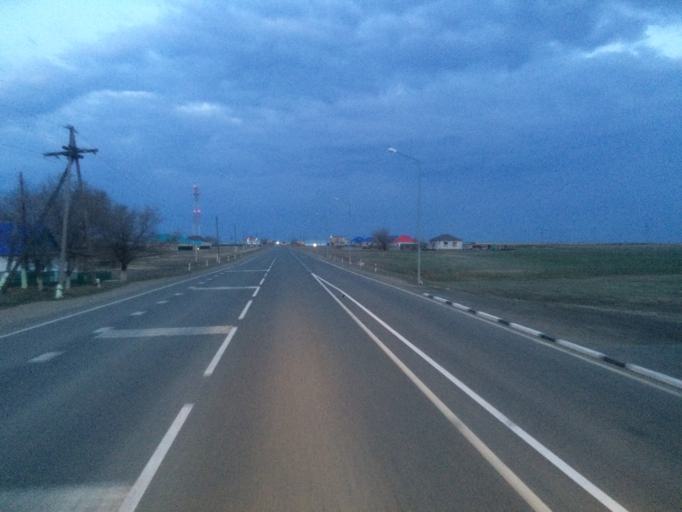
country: KZ
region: Aqtoebe
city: Martuk
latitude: 50.6385
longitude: 56.6950
